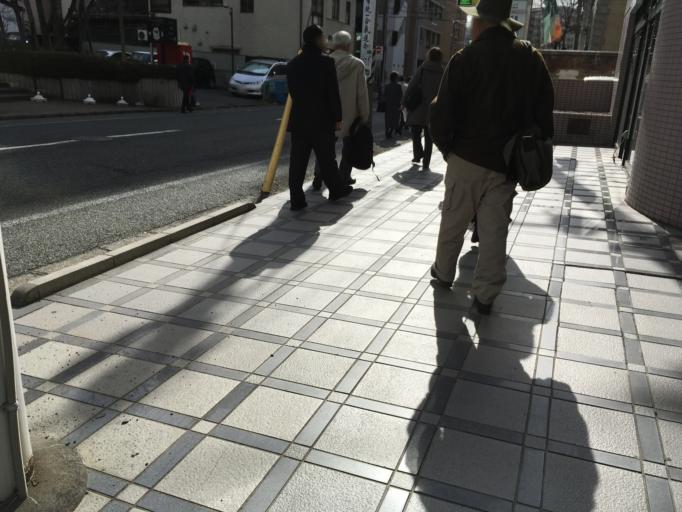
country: JP
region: Iwate
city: Morioka-shi
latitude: 39.6999
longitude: 141.1548
